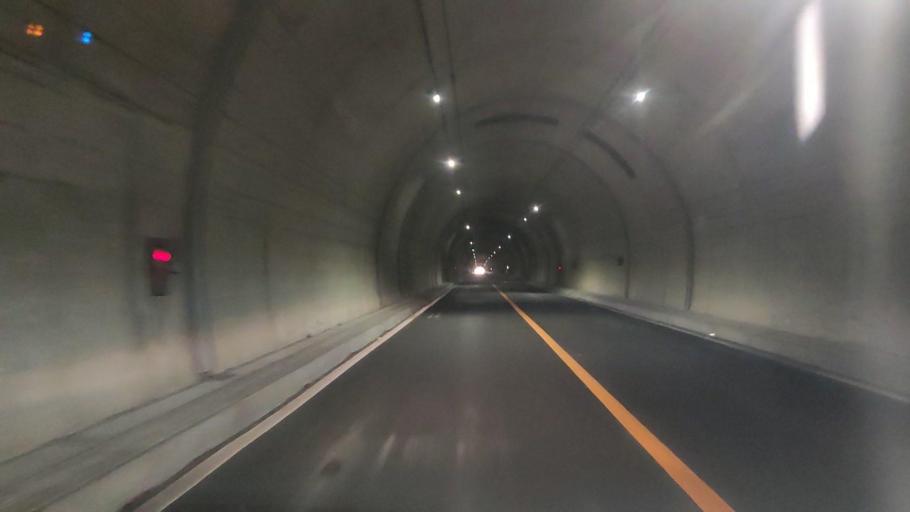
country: JP
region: Oita
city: Saiki
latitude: 32.8805
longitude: 131.9481
